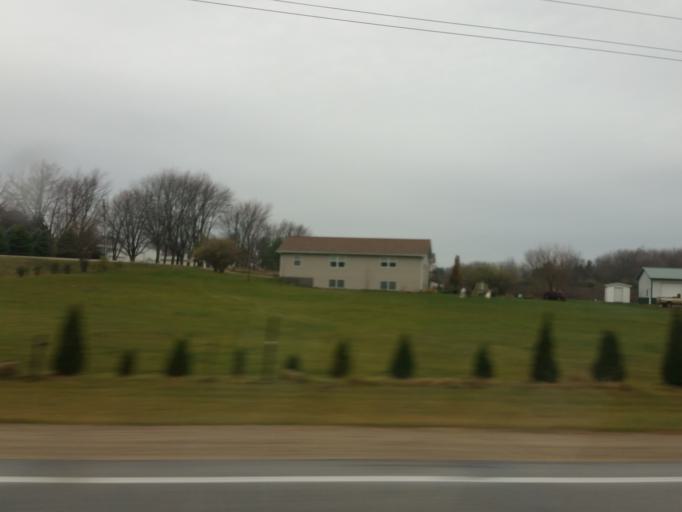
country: US
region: Iowa
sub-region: Black Hawk County
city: Elk Run Heights
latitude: 42.3852
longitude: -92.2462
